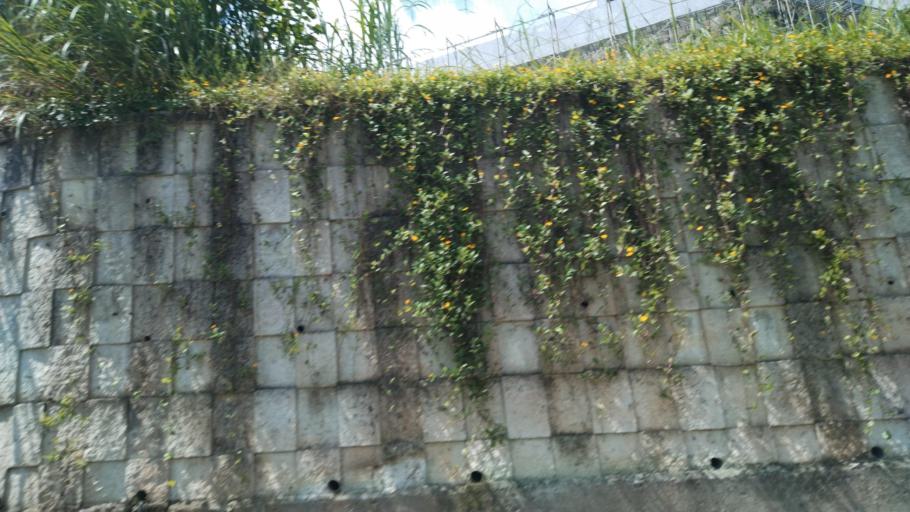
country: TW
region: Taipei
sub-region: Taipei
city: Banqiao
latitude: 24.9402
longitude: 121.5053
